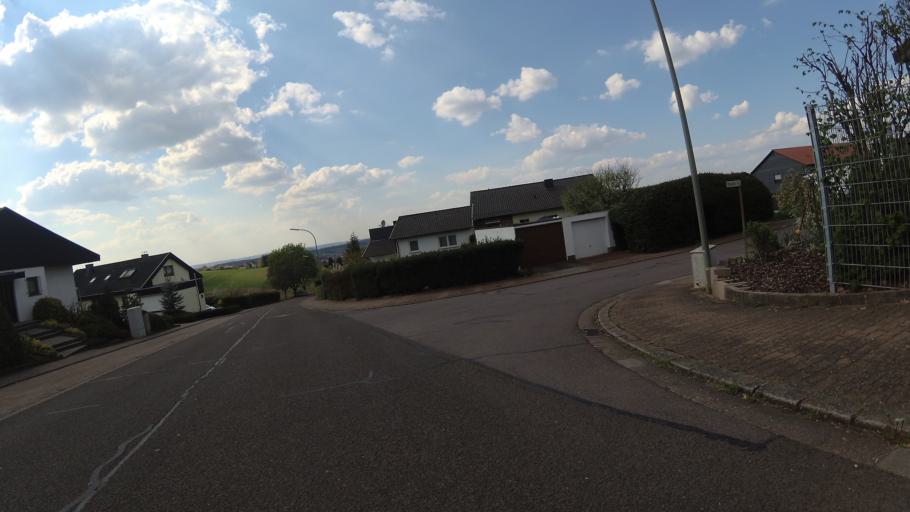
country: DE
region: Saarland
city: Riegelsberg
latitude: 49.2943
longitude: 6.9266
